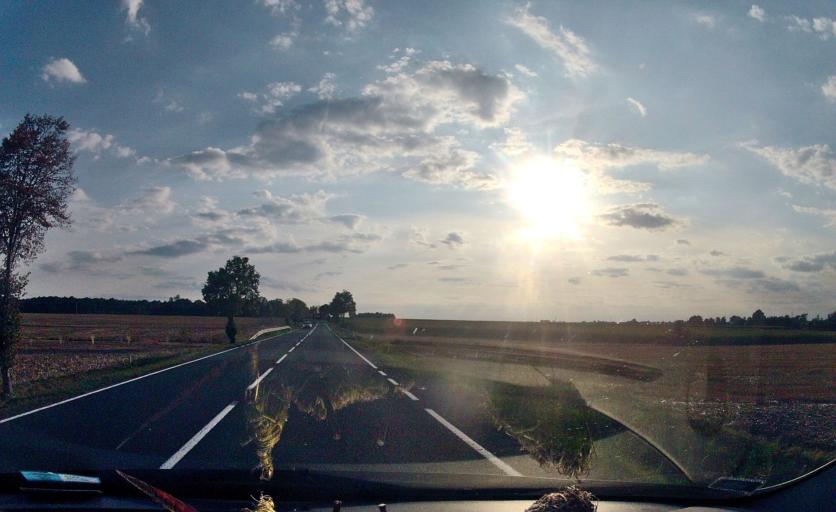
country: PL
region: Opole Voivodeship
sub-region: Powiat kluczborski
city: Kluczbork
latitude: 50.9978
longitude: 18.3067
